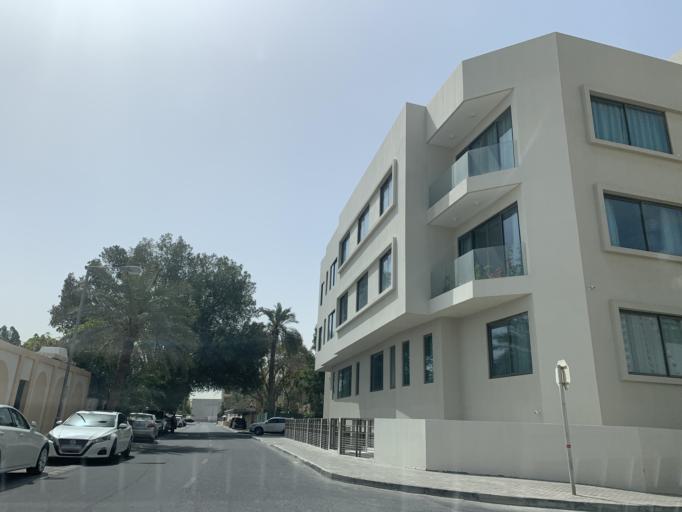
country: BH
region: Manama
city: Jidd Hafs
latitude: 26.2174
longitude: 50.5610
